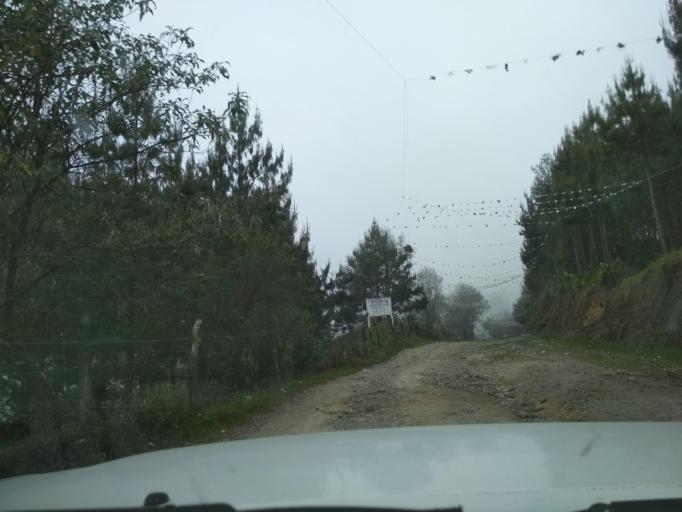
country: MX
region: Veracruz
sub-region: La Perla
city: Chilapa
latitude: 18.9820
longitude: -97.1947
